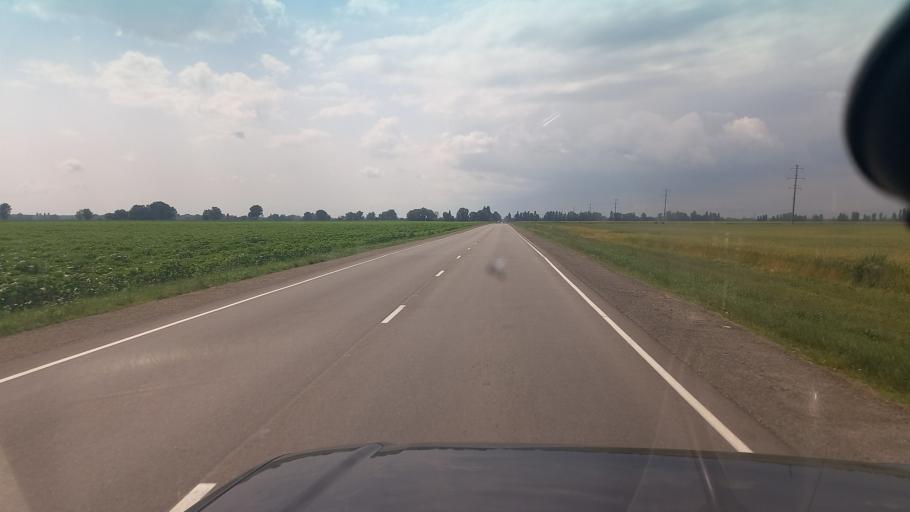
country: RU
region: Adygeya
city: Koshekhabl'
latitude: 44.9068
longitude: 40.4613
